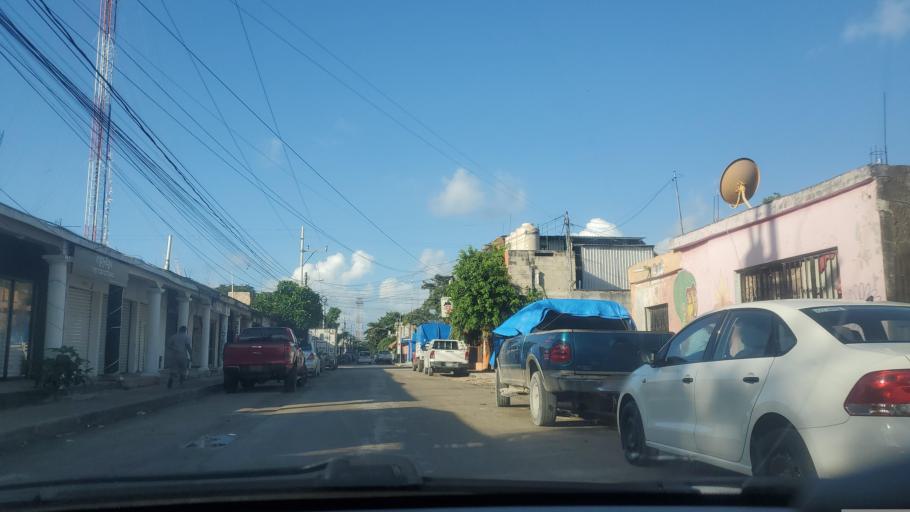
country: MX
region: Quintana Roo
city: Tulum
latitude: 20.2114
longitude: -87.4573
